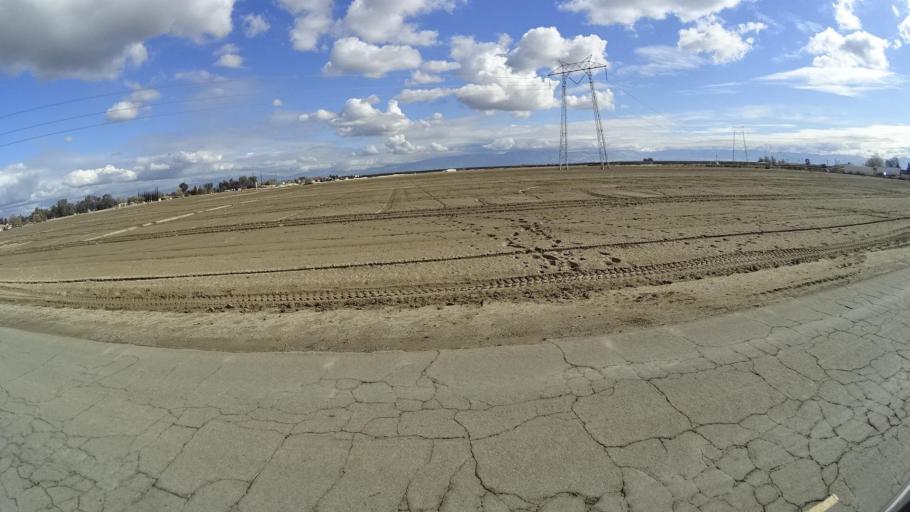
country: US
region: California
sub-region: Kern County
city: Greenfield
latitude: 35.2197
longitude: -119.0928
